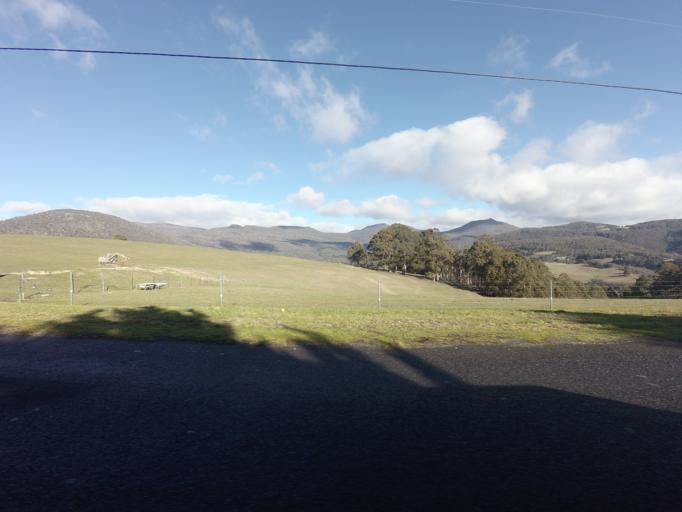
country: AU
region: Tasmania
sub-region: Glenorchy
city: Berriedale
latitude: -42.8291
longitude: 147.2011
